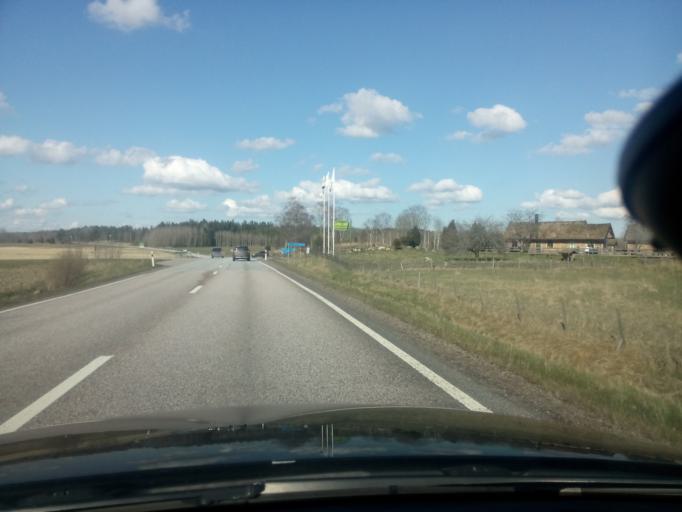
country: SE
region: Soedermanland
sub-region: Strangnas Kommun
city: Akers Styckebruk
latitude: 59.2724
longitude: 16.9703
